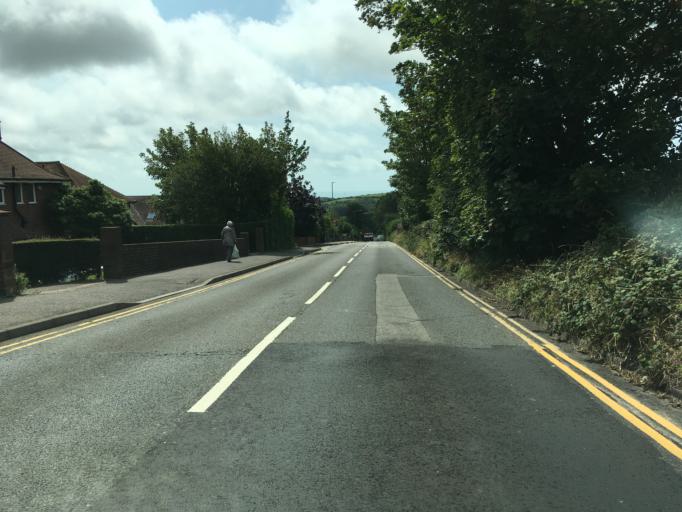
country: GB
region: England
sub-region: Brighton and Hove
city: Rottingdean
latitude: 50.8358
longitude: -0.0753
